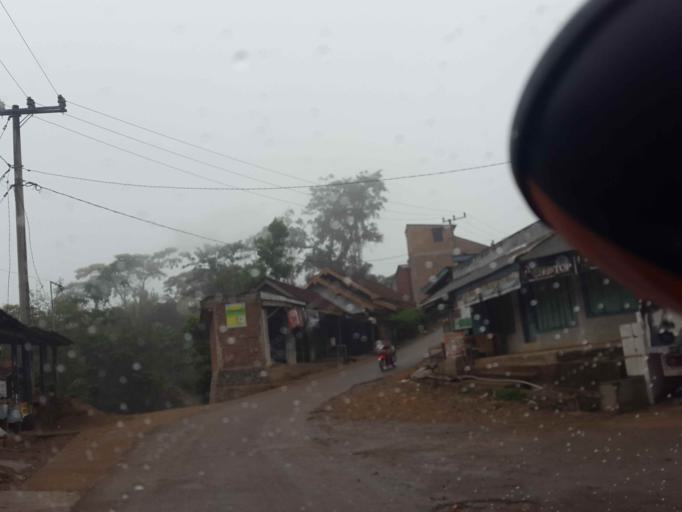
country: ID
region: East Java
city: Bangil
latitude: -8.1245
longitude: 111.3416
